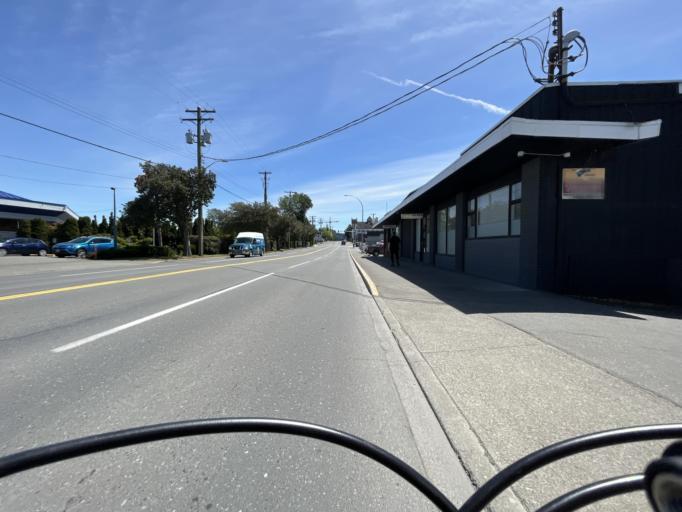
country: CA
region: British Columbia
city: Victoria
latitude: 48.4400
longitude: -123.3719
